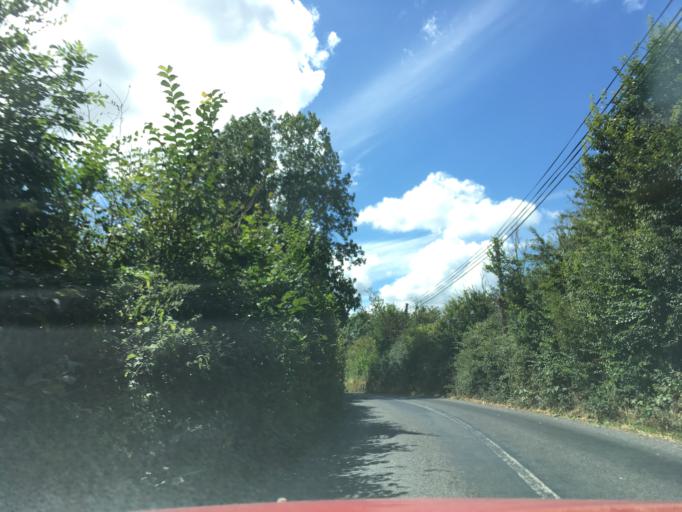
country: IE
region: Munster
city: Cahir
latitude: 52.3392
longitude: -7.9606
